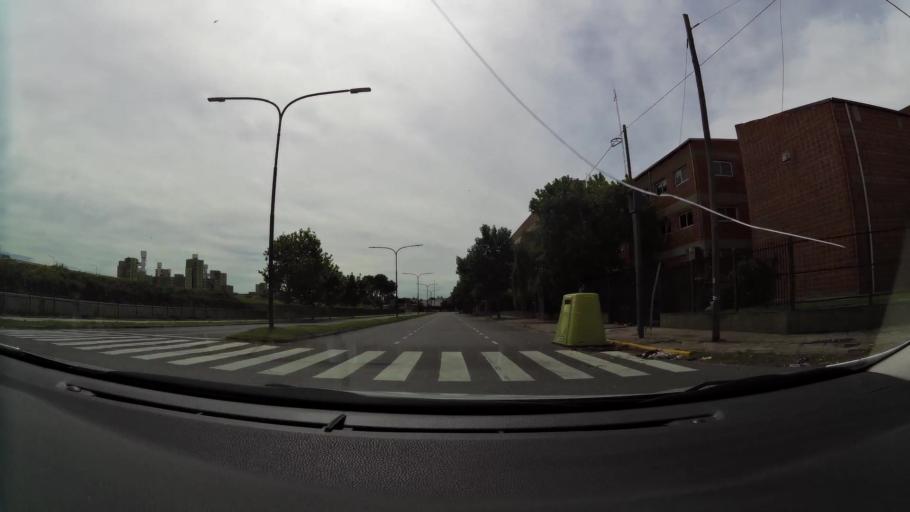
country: AR
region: Buenos Aires F.D.
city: Villa Lugano
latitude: -34.6673
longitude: -58.4380
